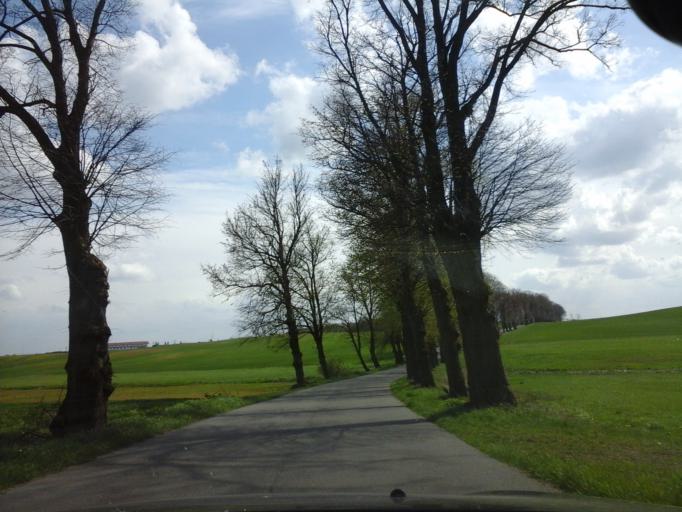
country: PL
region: West Pomeranian Voivodeship
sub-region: Powiat choszczenski
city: Pelczyce
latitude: 53.0938
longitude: 15.3504
